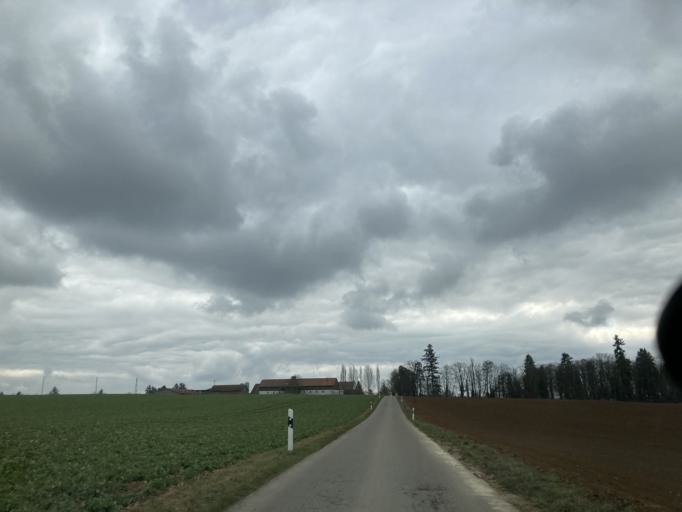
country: DE
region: Baden-Wuerttemberg
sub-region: Regierungsbezirk Stuttgart
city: Bondorf
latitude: 48.4538
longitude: 8.8192
